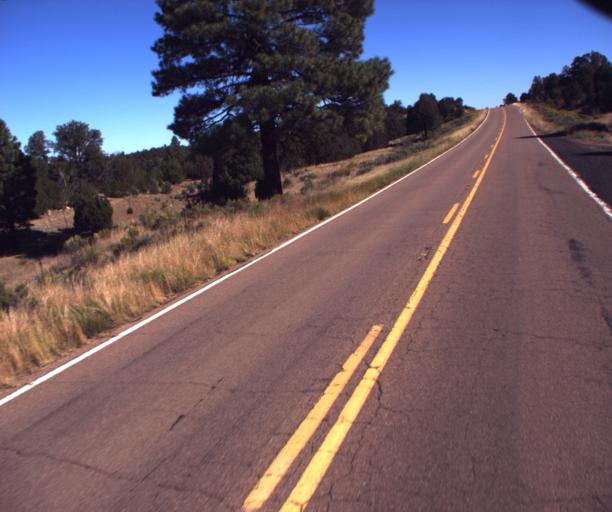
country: US
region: Arizona
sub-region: Navajo County
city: Heber-Overgaard
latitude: 34.4384
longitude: -110.5349
